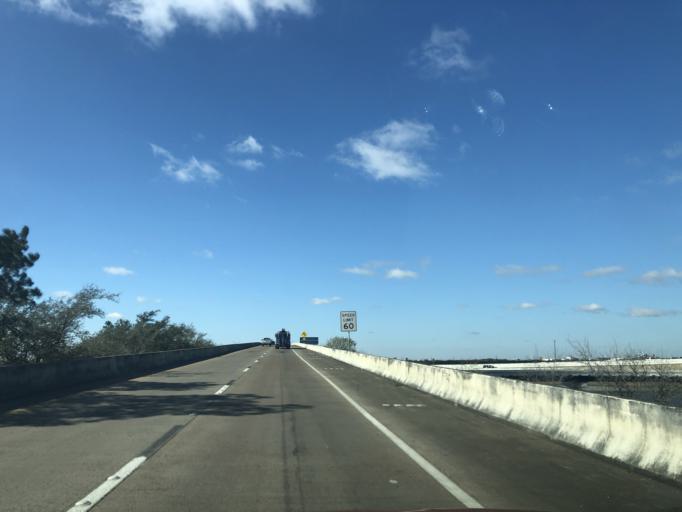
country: US
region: Texas
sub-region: Harris County
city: Baytown
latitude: 29.7139
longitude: -94.9973
